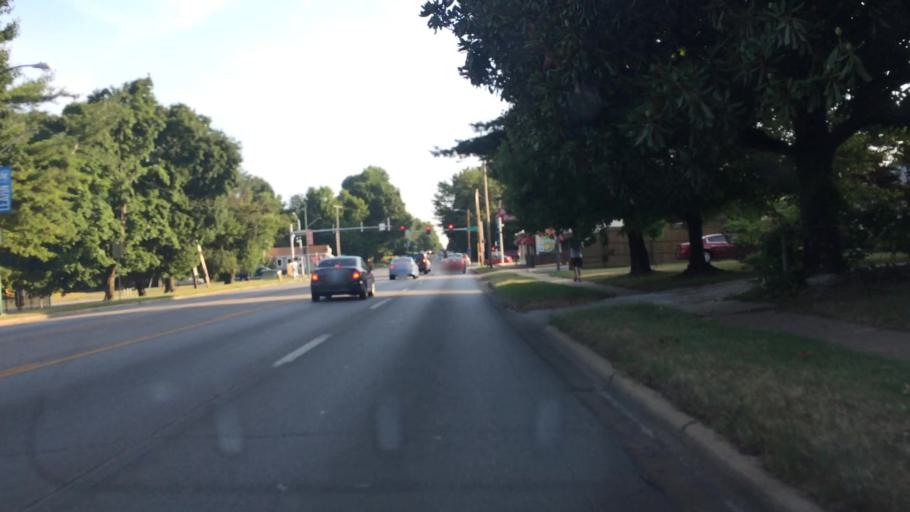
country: US
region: Missouri
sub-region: Greene County
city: Springfield
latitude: 37.1881
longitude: -93.2764
